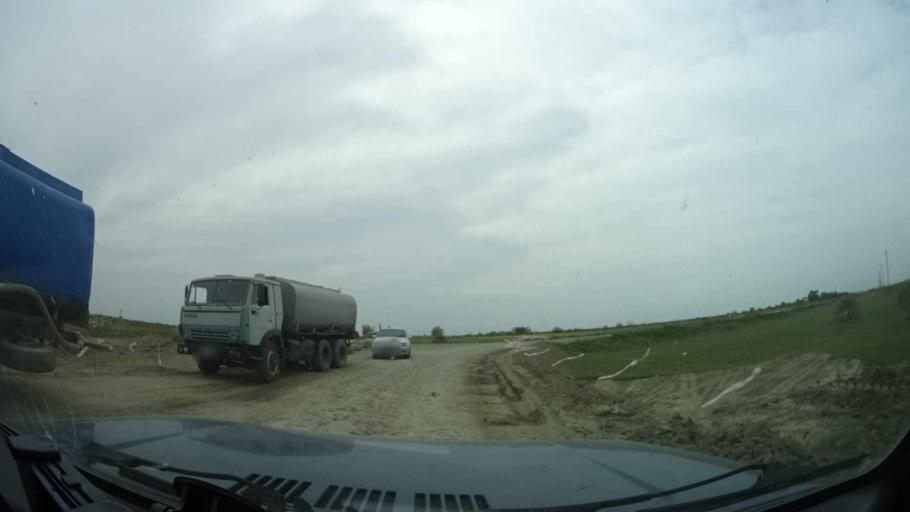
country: AZ
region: Imisli
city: Imishli
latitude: 39.6844
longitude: 48.1121
